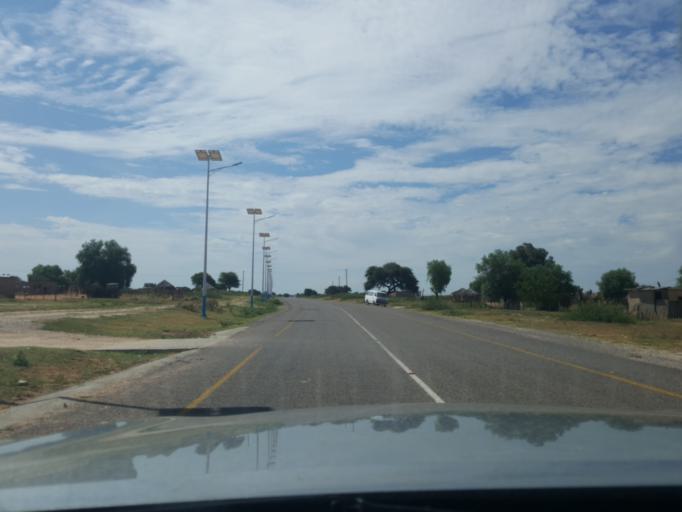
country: BW
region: Kweneng
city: Letlhakeng
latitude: -24.0834
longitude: 25.0310
